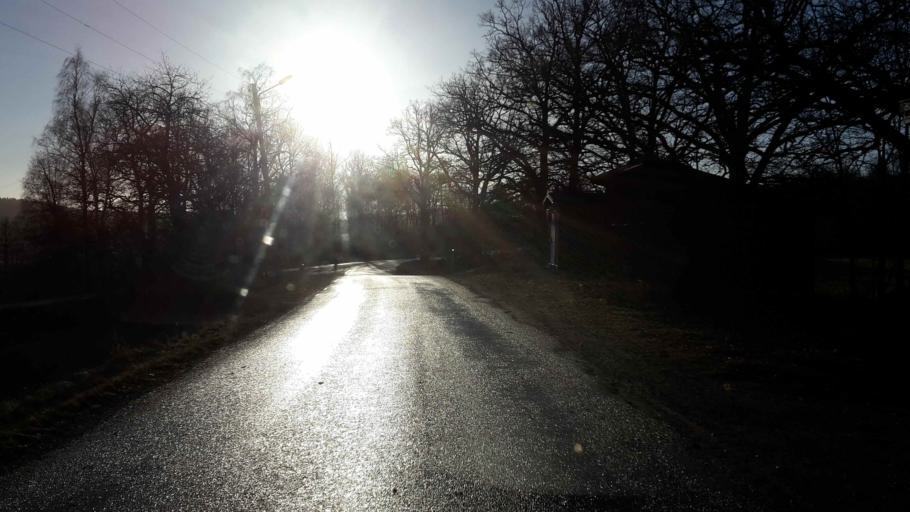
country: SE
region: Kalmar
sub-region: Vasterviks Kommun
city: Overum
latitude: 58.1517
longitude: 16.3244
